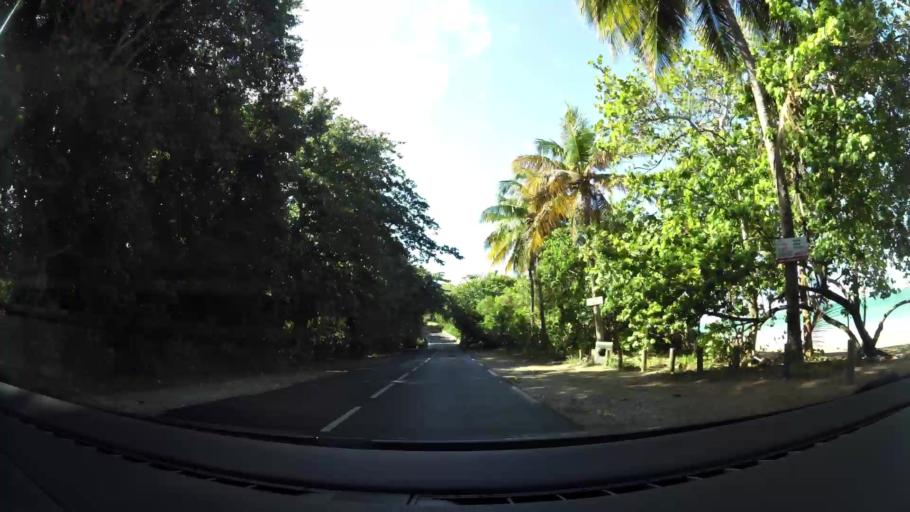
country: GP
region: Guadeloupe
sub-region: Guadeloupe
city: Sainte-Rose
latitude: 16.3539
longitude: -61.7565
